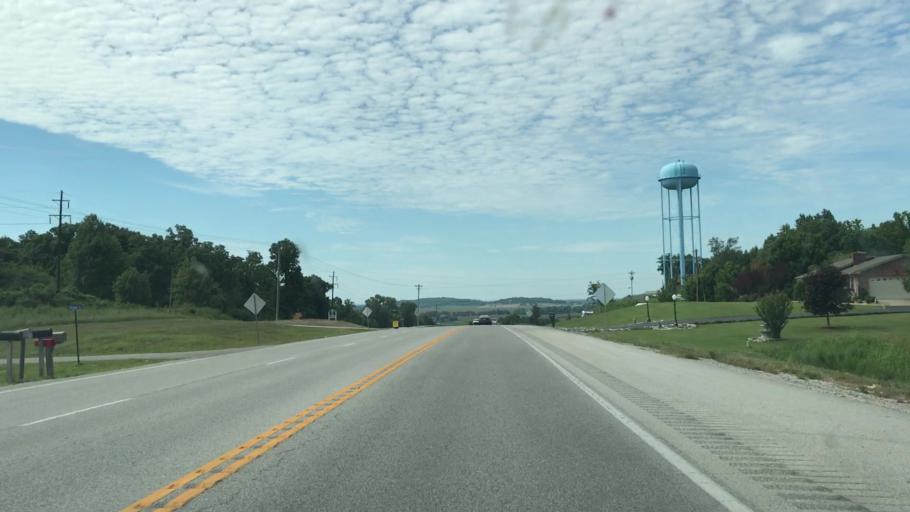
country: US
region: Kentucky
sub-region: Edmonson County
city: Brownsville
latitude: 37.1039
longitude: -86.2295
